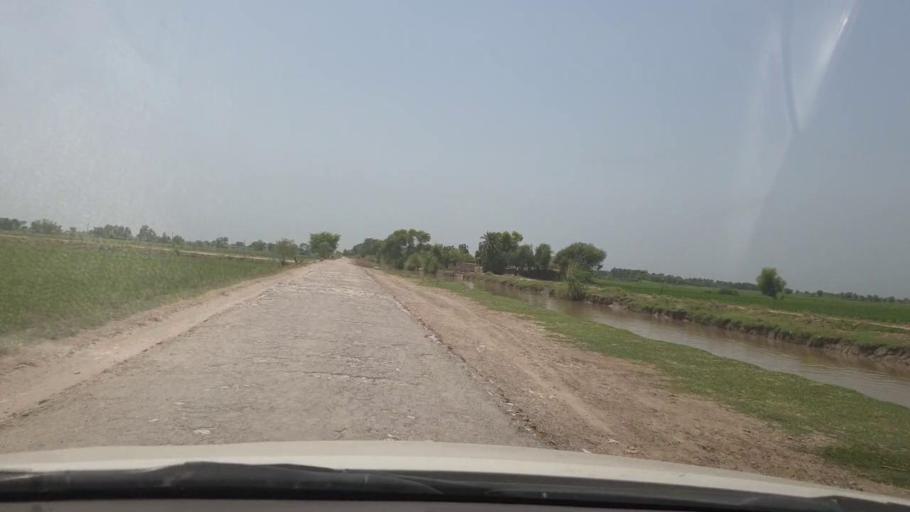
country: PK
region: Sindh
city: Shikarpur
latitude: 28.0907
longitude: 68.5711
